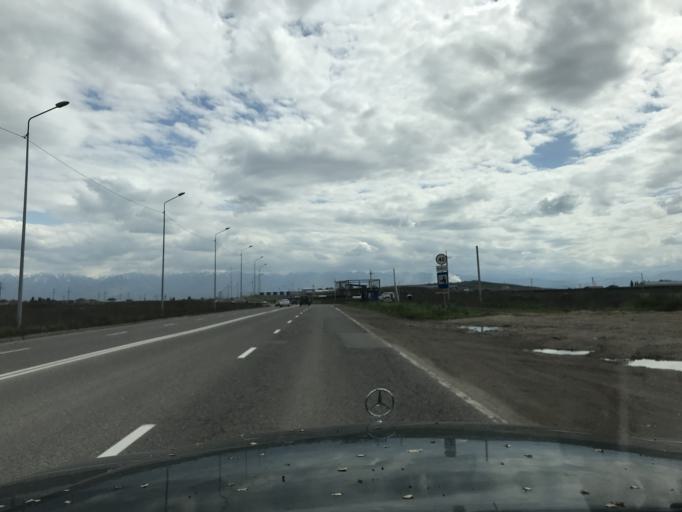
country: KZ
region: Almaty Oblysy
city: Burunday
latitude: 43.3504
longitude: 76.8341
